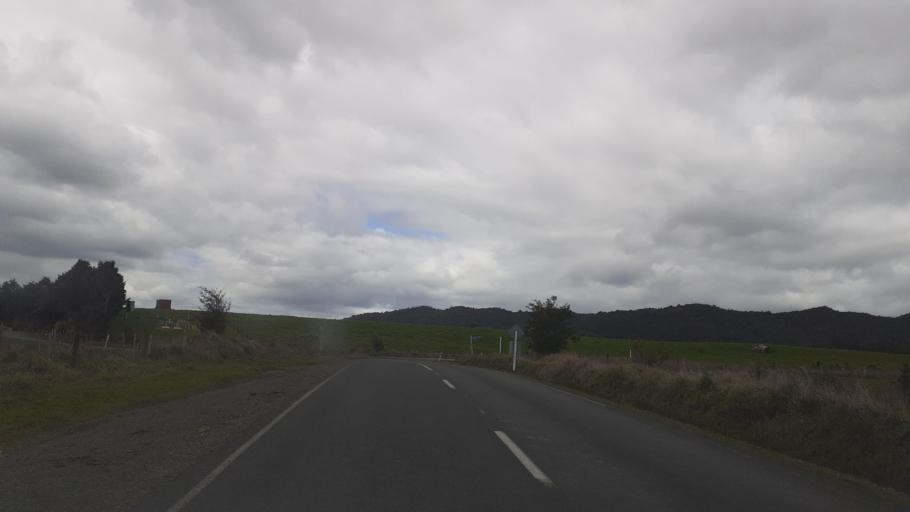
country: NZ
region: Northland
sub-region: Far North District
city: Moerewa
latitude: -35.5902
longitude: 173.9753
